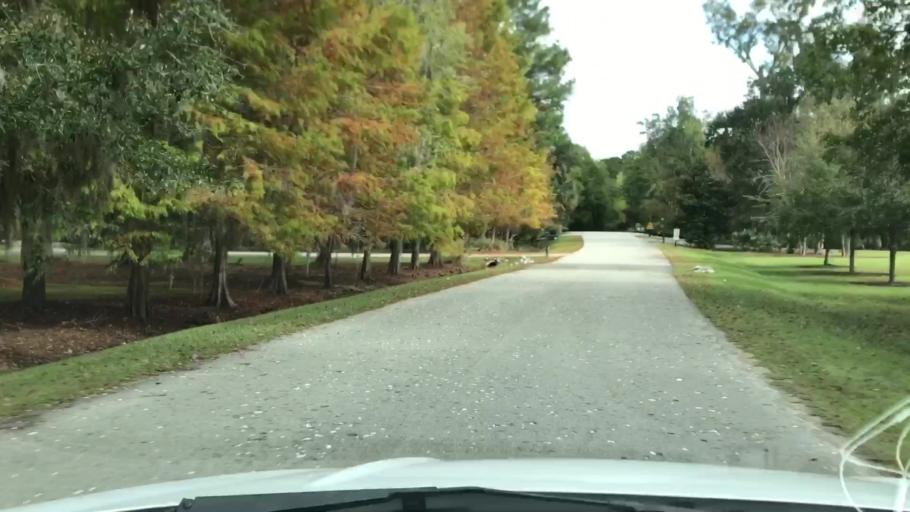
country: US
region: South Carolina
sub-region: Beaufort County
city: Bluffton
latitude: 32.2392
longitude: -80.9253
